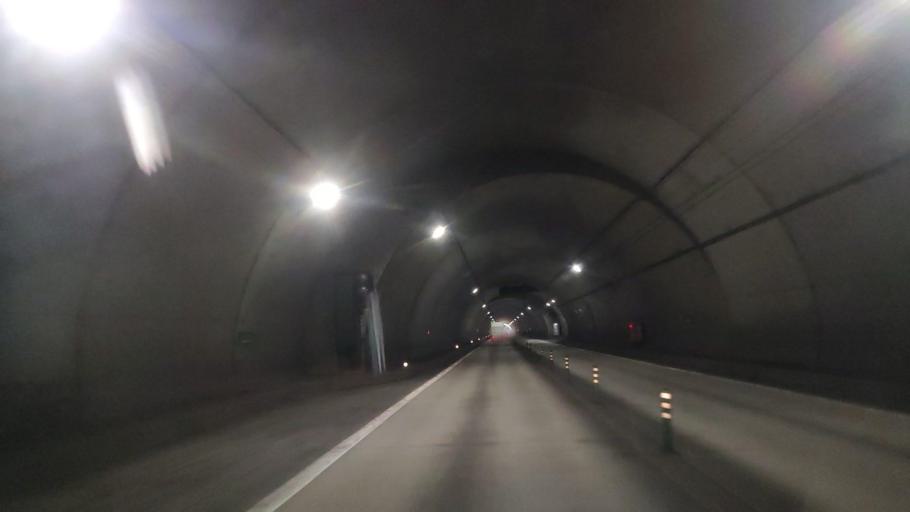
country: JP
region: Ishikawa
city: Nanao
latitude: 37.0188
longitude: 137.0102
